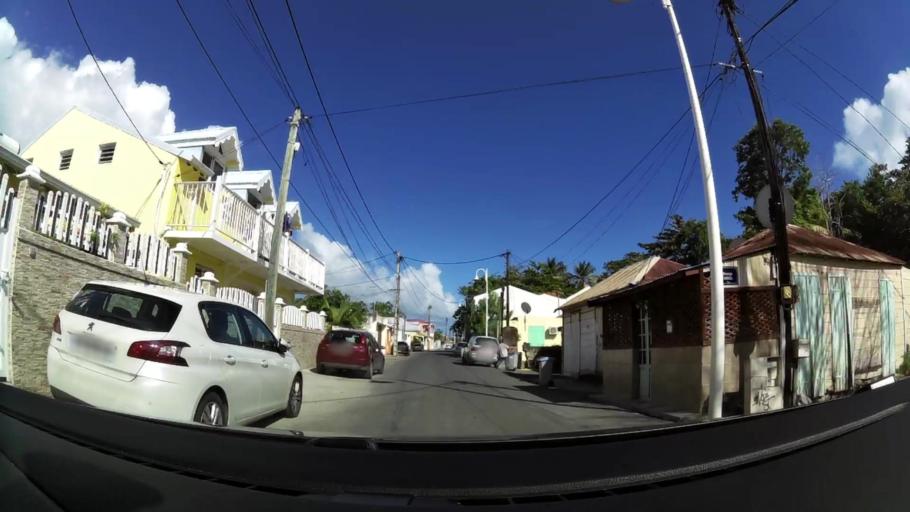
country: GP
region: Guadeloupe
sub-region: Guadeloupe
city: Sainte-Anne
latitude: 16.2248
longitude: -61.3821
